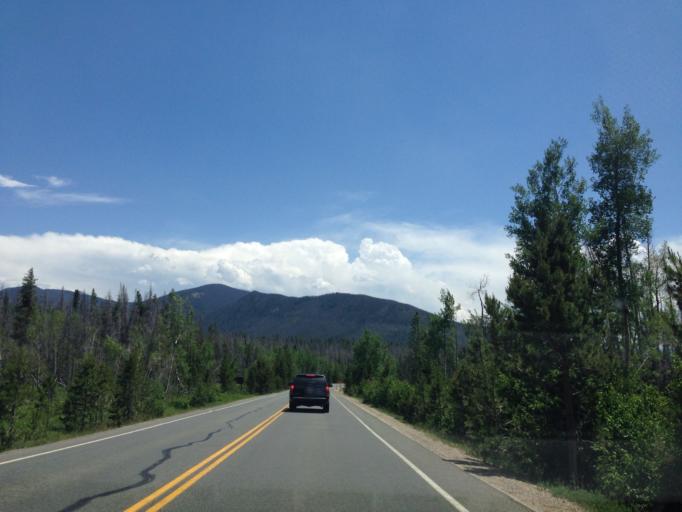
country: US
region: Colorado
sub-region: Grand County
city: Granby
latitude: 40.2636
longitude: -105.8320
